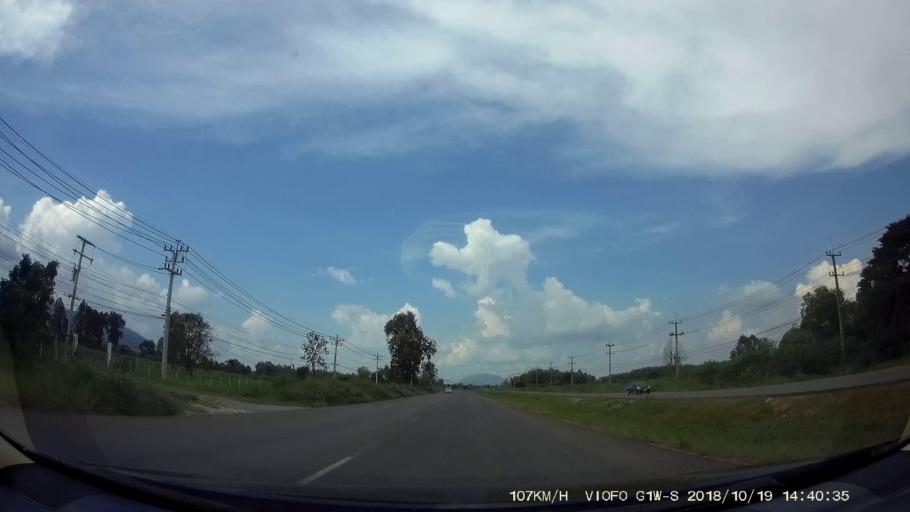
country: TH
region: Chaiyaphum
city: Kaeng Khro
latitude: 16.2430
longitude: 102.1964
